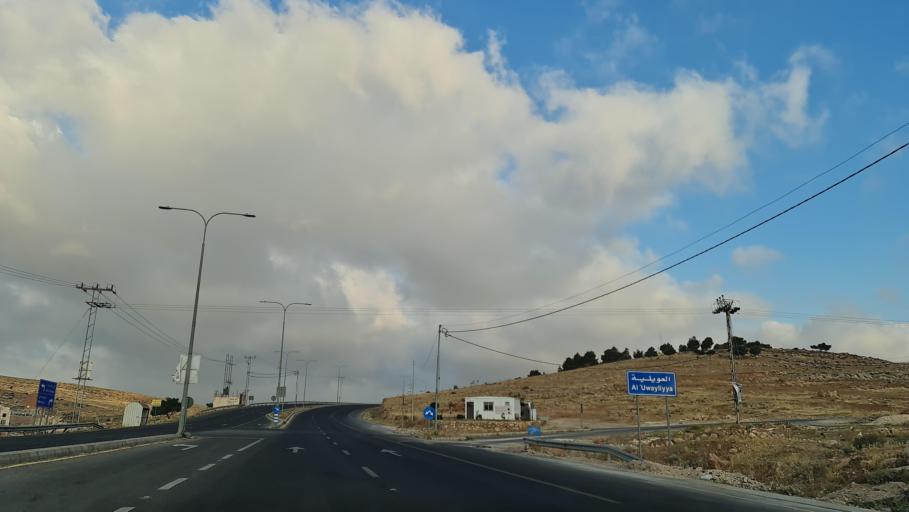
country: JO
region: Zarqa
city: Russeifa
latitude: 32.0924
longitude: 35.9732
